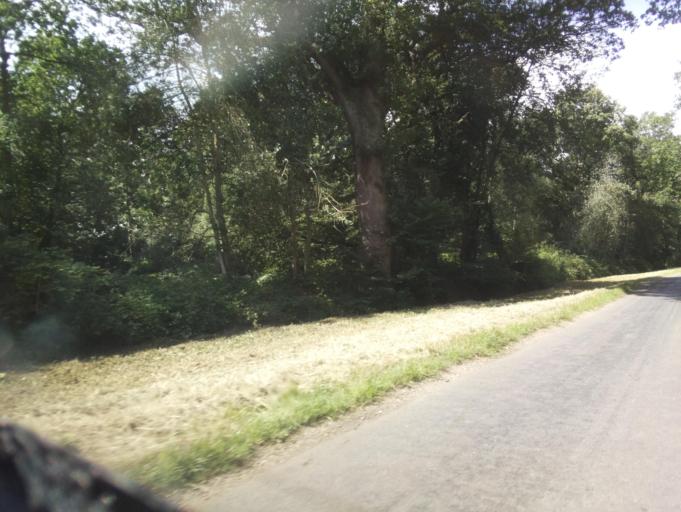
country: GB
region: England
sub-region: Wiltshire
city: Hankerton
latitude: 51.6208
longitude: -2.0088
